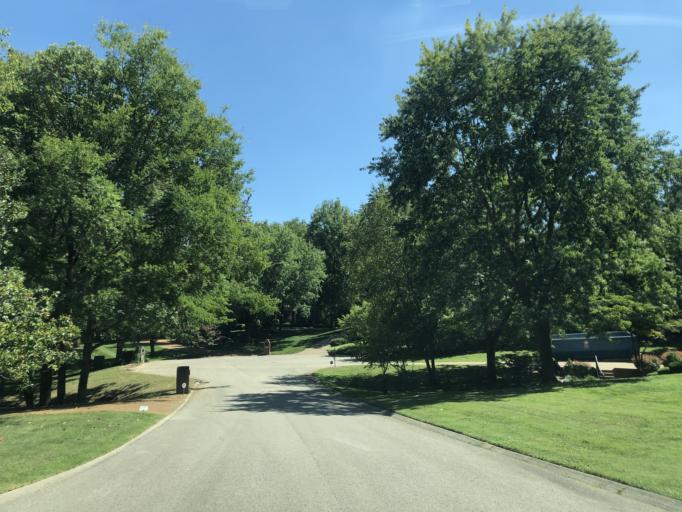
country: US
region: Tennessee
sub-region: Davidson County
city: Oak Hill
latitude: 36.0715
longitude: -86.7799
